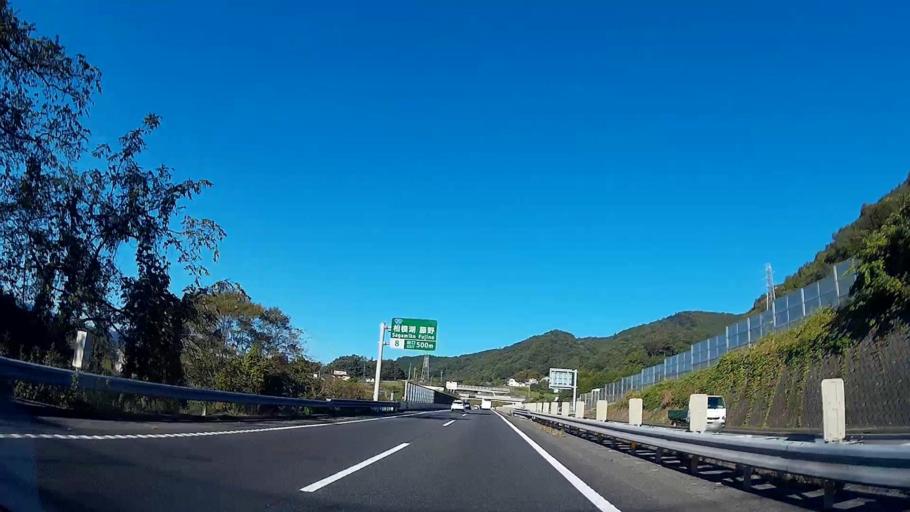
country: JP
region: Yamanashi
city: Uenohara
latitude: 35.6219
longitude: 139.1761
